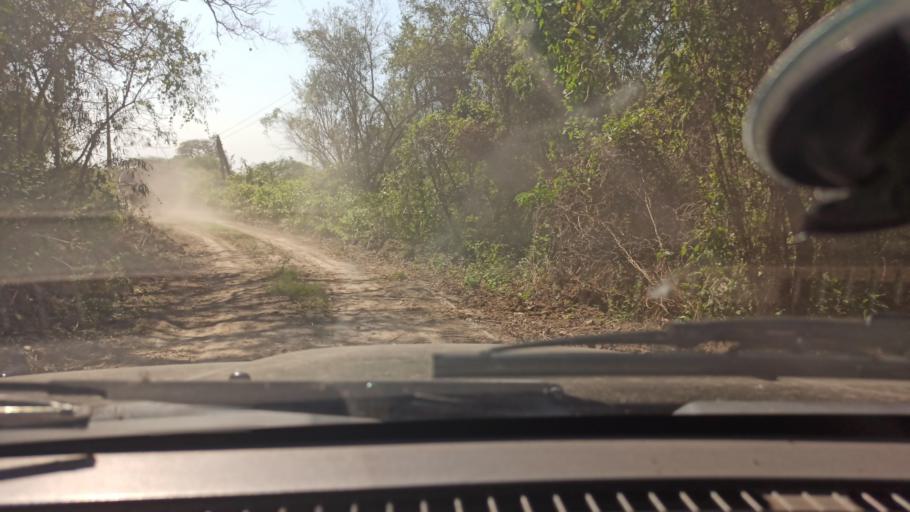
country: PY
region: Asuncion
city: Asuncion
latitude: -25.3489
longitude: -57.6701
